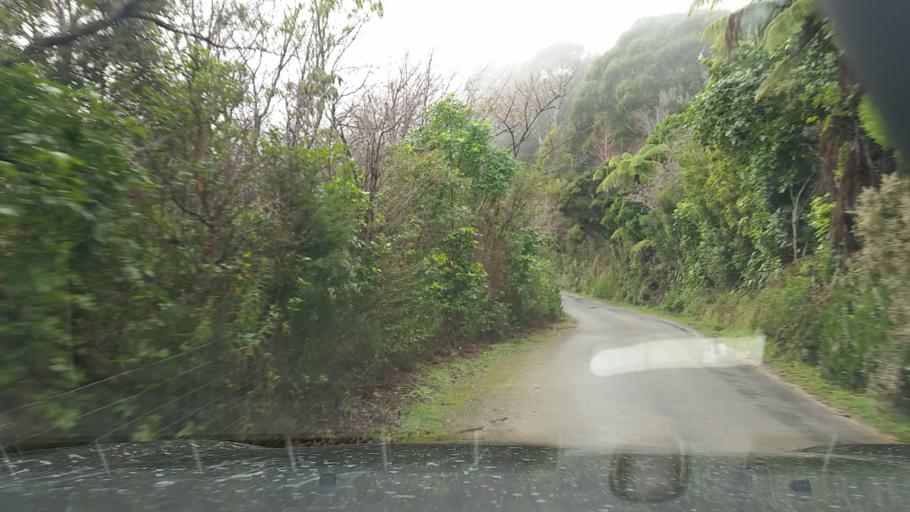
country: NZ
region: Marlborough
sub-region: Marlborough District
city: Picton
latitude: -41.1697
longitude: 174.0475
